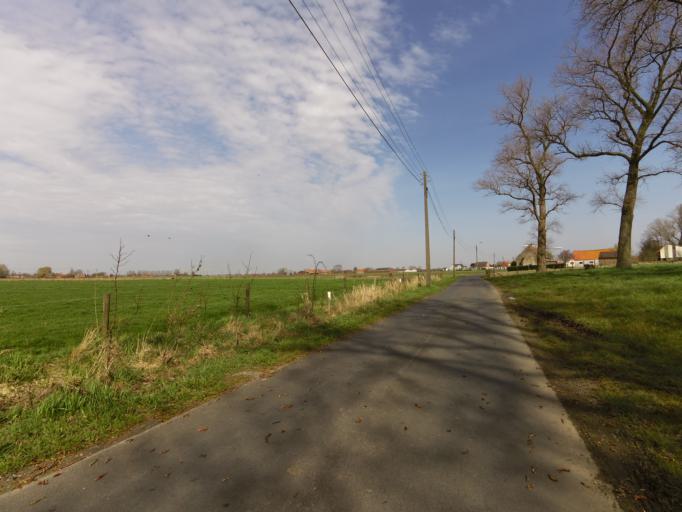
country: BE
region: Flanders
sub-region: Provincie West-Vlaanderen
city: Koekelare
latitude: 51.1055
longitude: 2.9435
